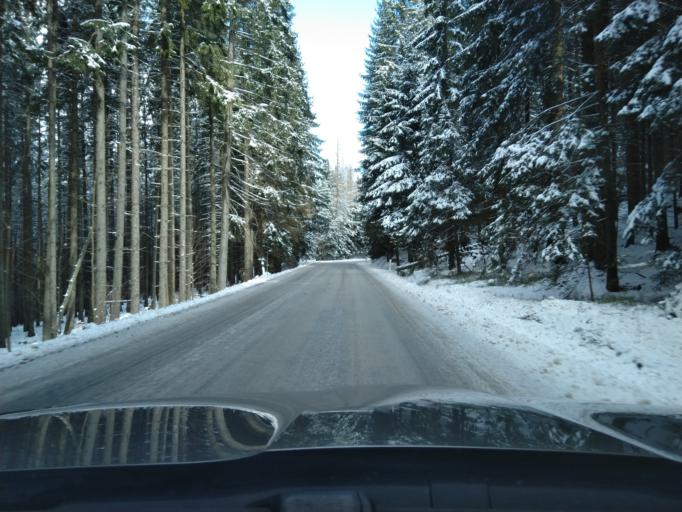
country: CZ
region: Jihocesky
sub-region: Okres Prachatice
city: Zdikov
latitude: 49.0559
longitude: 13.6951
